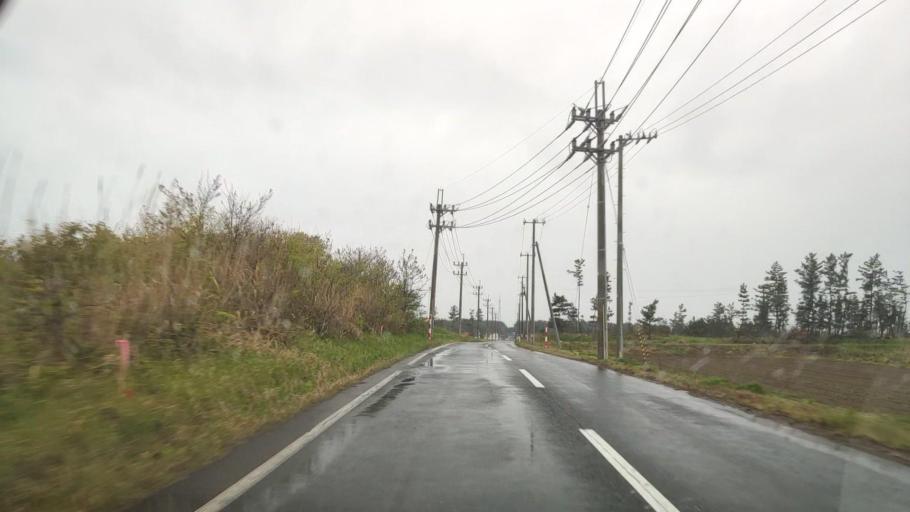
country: JP
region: Akita
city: Noshiromachi
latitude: 40.0958
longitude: 139.9727
